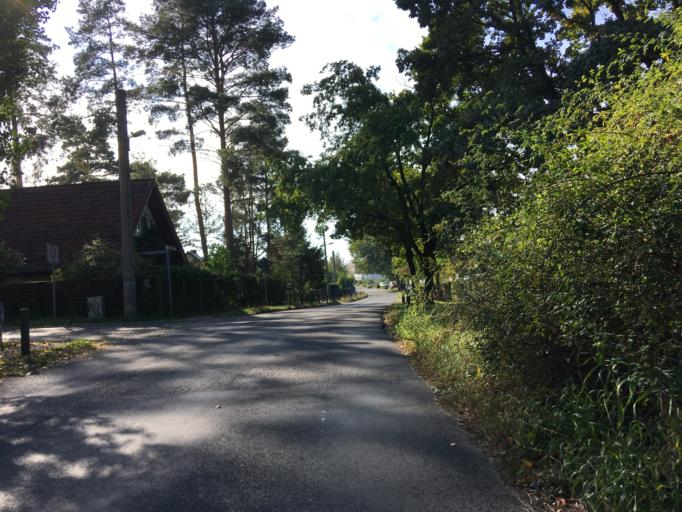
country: DE
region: Brandenburg
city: Neuenhagen
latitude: 52.5207
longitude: 13.7144
